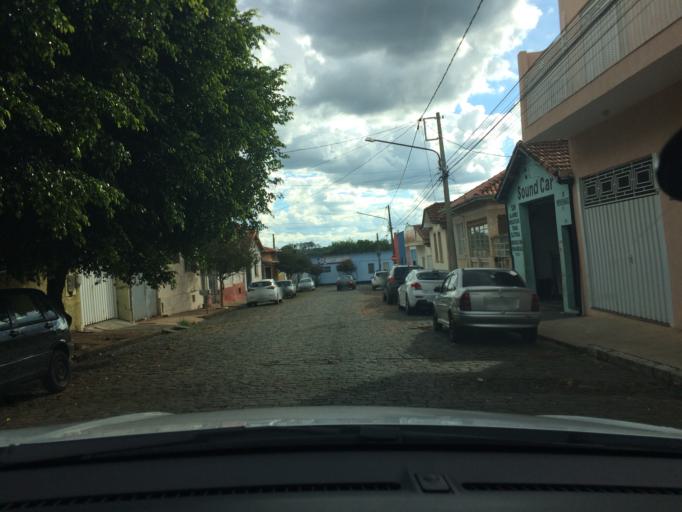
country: BR
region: Sao Paulo
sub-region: Casa Branca
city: Casa Branca
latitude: -21.7790
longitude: -47.0805
